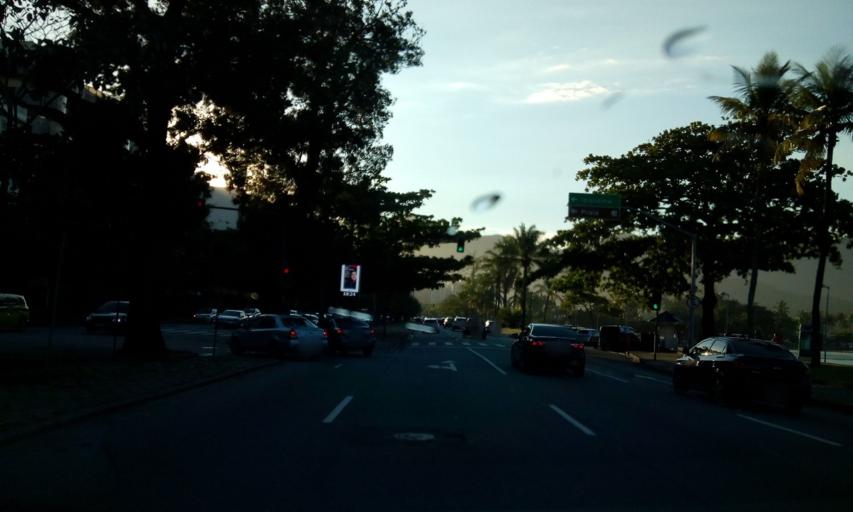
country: BR
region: Rio de Janeiro
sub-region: Rio De Janeiro
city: Rio de Janeiro
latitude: -22.9806
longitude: -43.2086
